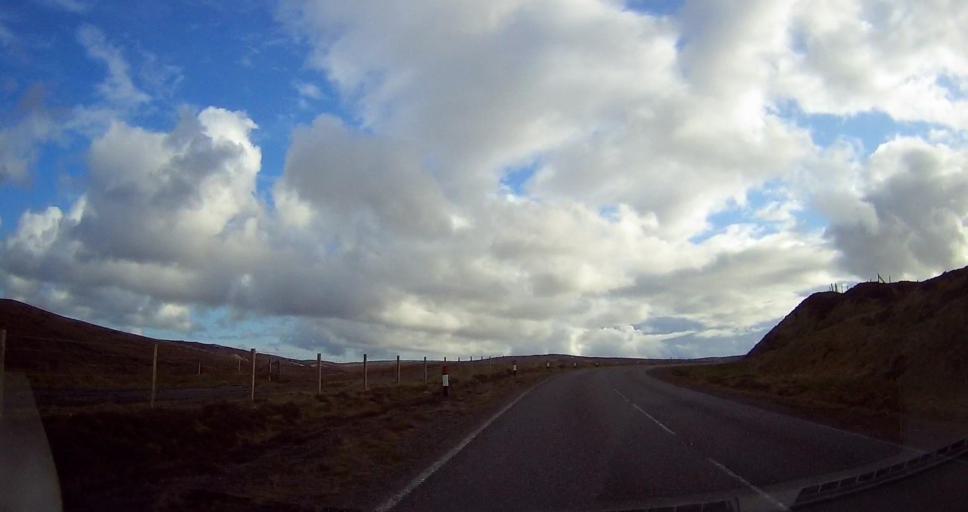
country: GB
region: Scotland
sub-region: Shetland Islands
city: Lerwick
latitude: 60.3512
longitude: -1.2062
